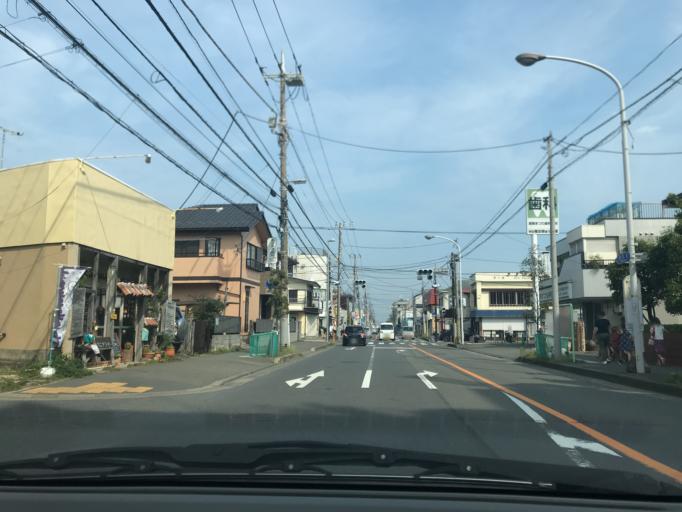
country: JP
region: Kanagawa
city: Chigasaki
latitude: 35.3250
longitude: 139.4140
